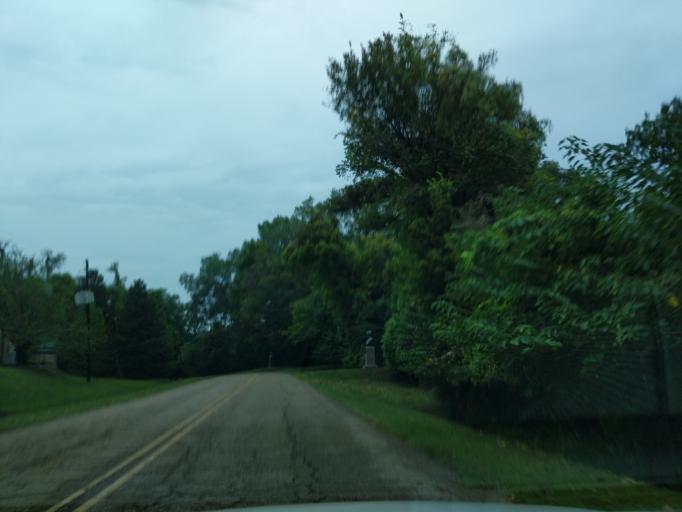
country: US
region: Mississippi
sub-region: Warren County
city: Vicksburg
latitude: 32.3180
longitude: -90.8898
